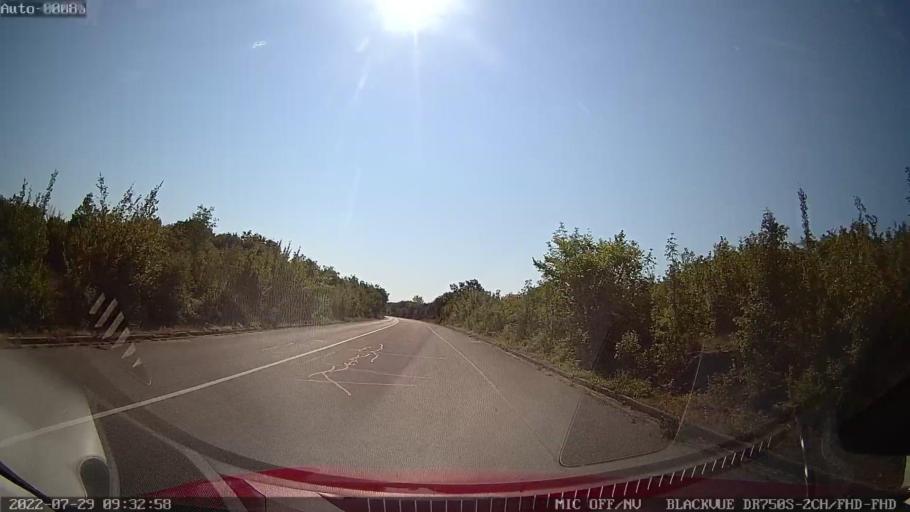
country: HR
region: Zadarska
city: Obrovac
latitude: 44.1801
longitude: 15.7193
